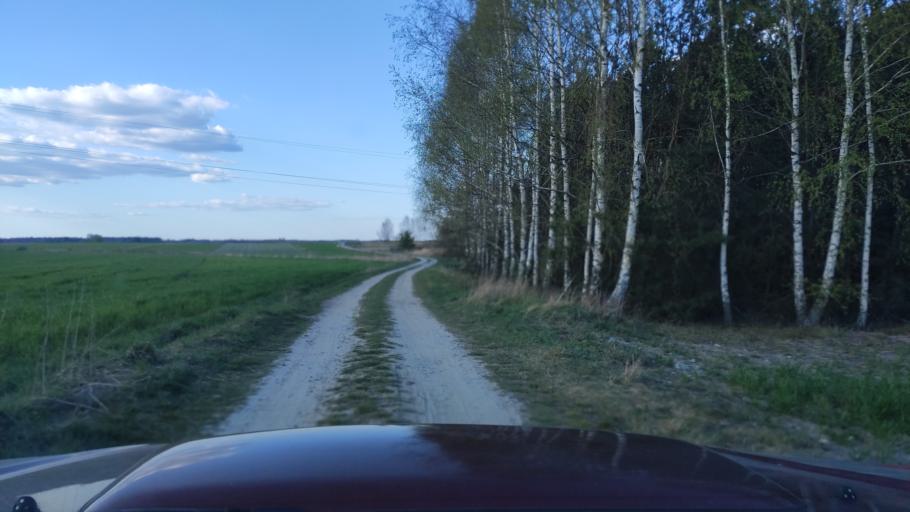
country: PL
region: Masovian Voivodeship
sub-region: Powiat zwolenski
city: Zwolen
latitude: 51.3706
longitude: 21.5749
